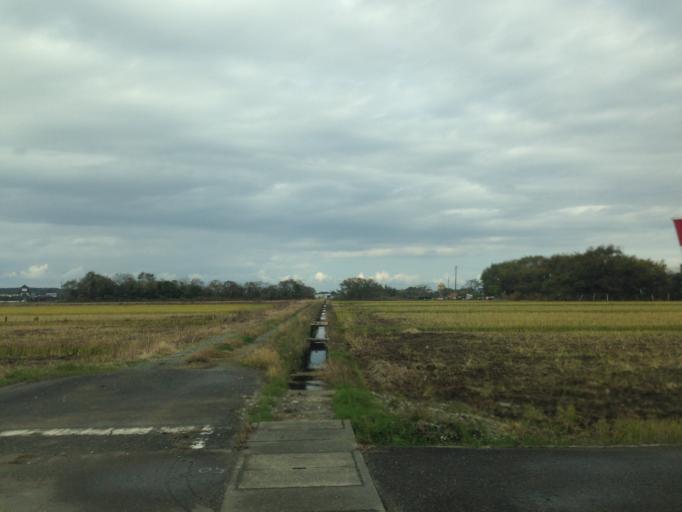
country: JP
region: Ishikawa
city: Komatsu
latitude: 36.2997
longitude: 136.3674
